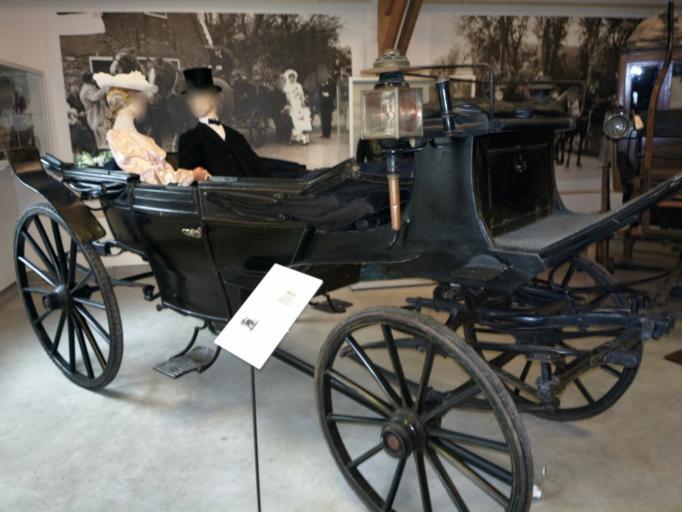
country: NL
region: North Holland
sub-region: Gemeente Texel
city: Den Burg
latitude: 53.0722
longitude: 4.8216
